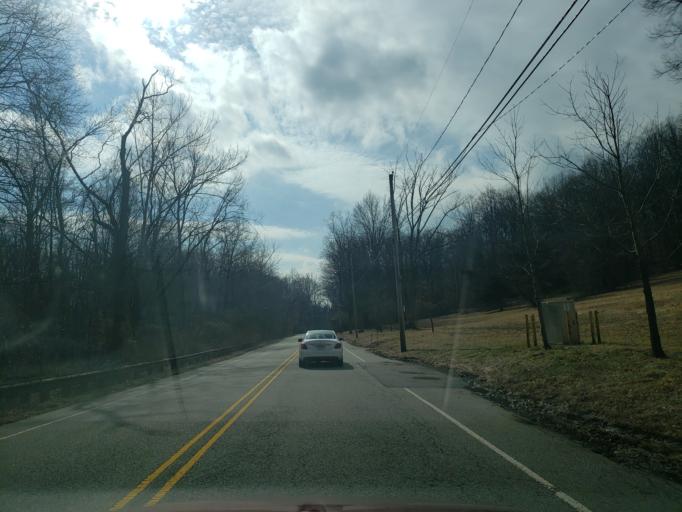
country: US
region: New Jersey
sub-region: Essex County
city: Short Hills
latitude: 40.7510
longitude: -74.2985
